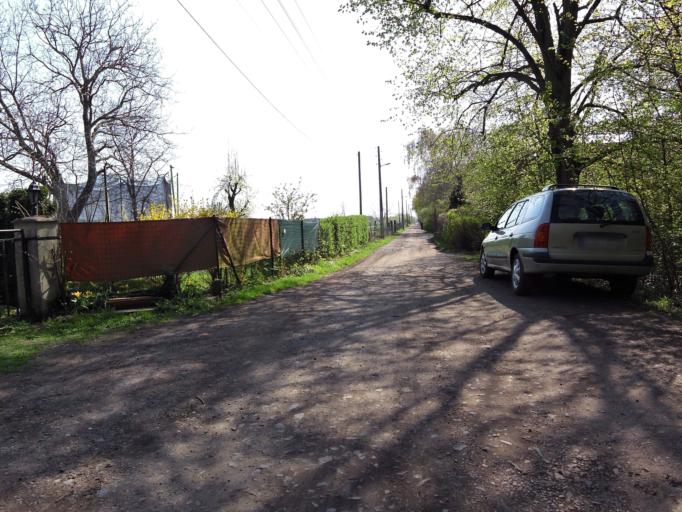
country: DE
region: Saxony
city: Rackwitz
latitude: 51.3982
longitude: 12.3168
